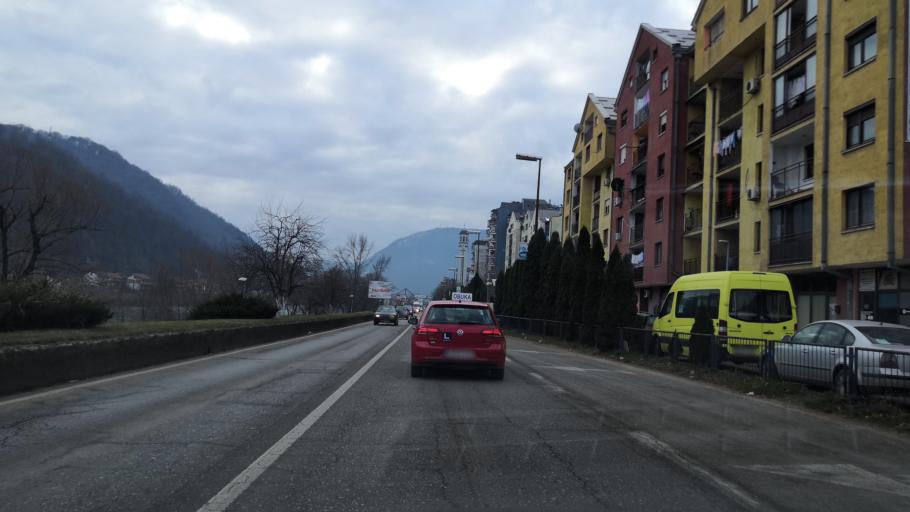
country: BA
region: Republika Srpska
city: Zvornik
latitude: 44.3924
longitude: 19.1058
